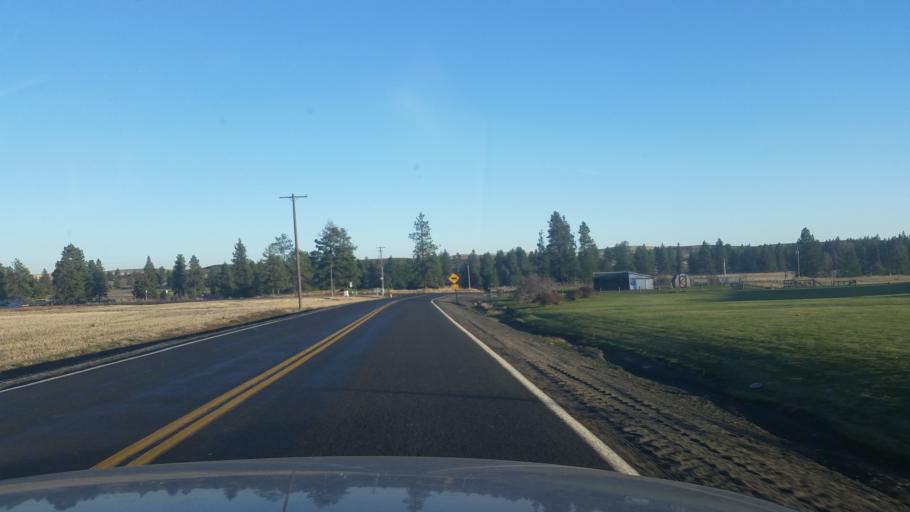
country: US
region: Washington
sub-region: Spokane County
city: Opportunity
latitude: 47.3848
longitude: -117.3184
